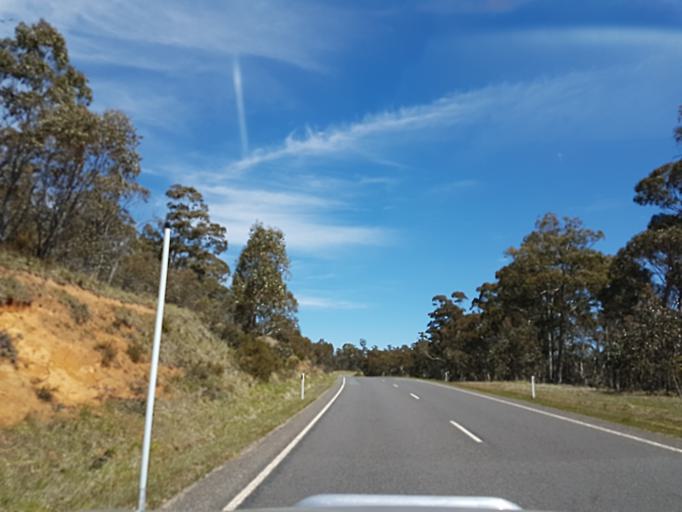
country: AU
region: Victoria
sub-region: Alpine
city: Mount Beauty
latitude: -37.0813
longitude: 147.3659
